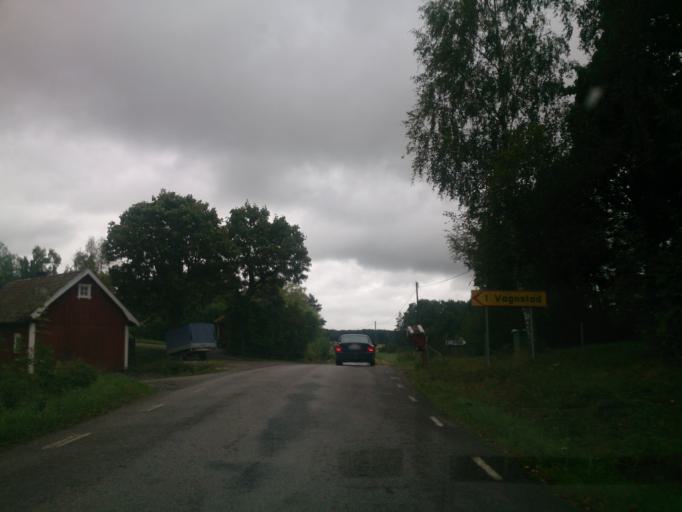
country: SE
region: OEstergoetland
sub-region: Norrkopings Kommun
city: Krokek
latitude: 58.5467
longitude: 16.5988
